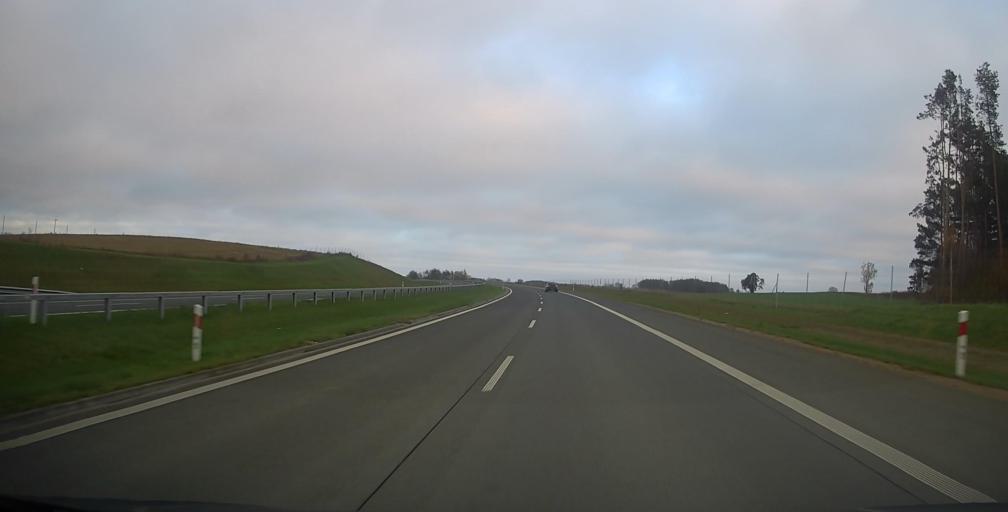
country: PL
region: Podlasie
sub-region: Powiat grajewski
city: Szczuczyn
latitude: 53.5198
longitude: 22.2580
